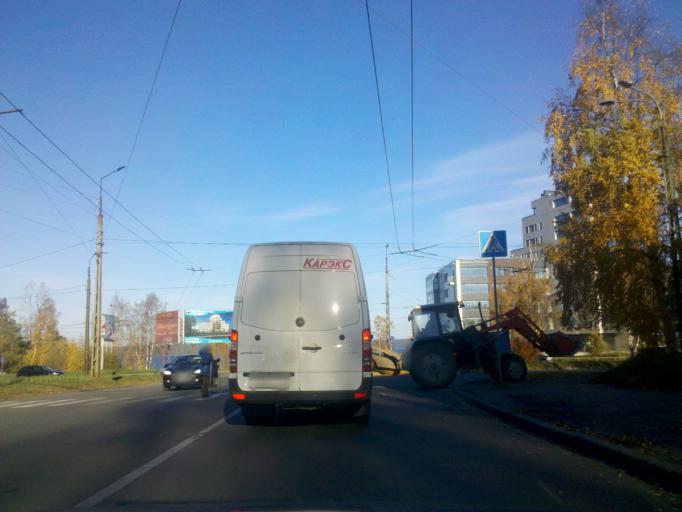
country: RU
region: Republic of Karelia
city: Petrozavodsk
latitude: 61.7992
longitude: 34.3591
